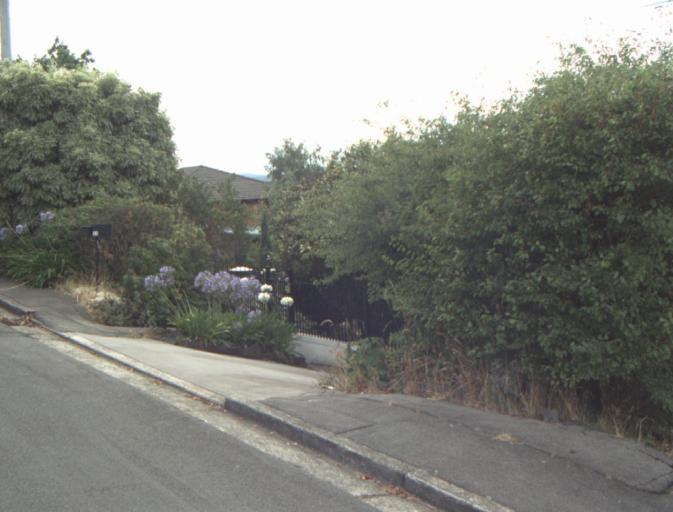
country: AU
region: Tasmania
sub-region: Launceston
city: Launceston
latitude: -41.4340
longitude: 147.1147
